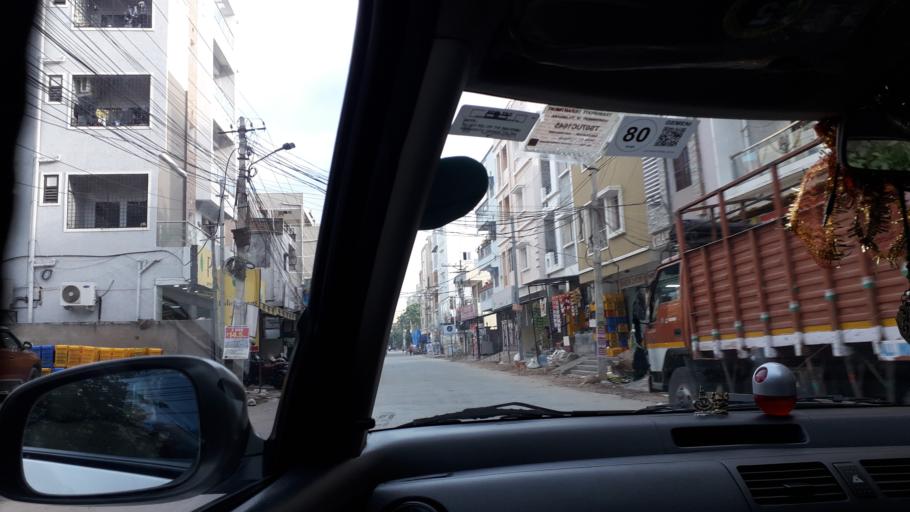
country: IN
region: Telangana
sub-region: Hyderabad
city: Hyderabad
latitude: 17.3963
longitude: 78.3774
